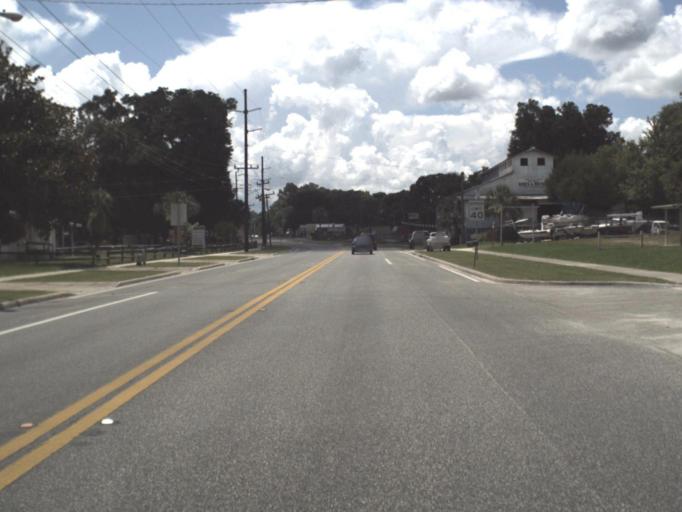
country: US
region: Florida
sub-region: Putnam County
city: Crescent City
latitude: 29.4985
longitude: -81.5971
